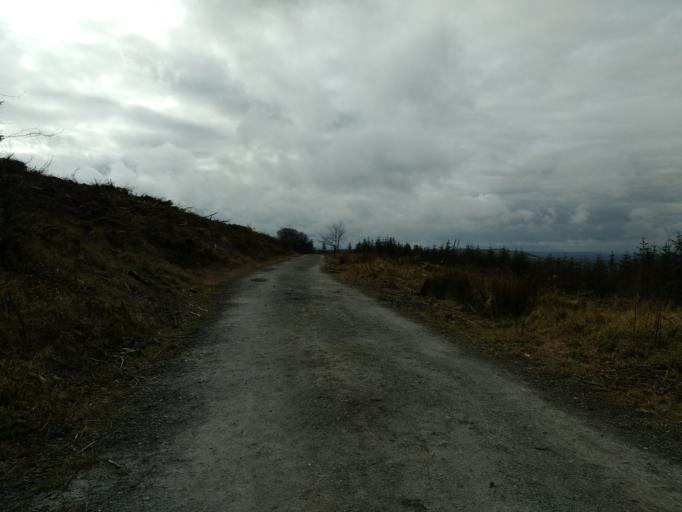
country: IE
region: Leinster
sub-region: Kilkenny
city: Callan
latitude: 52.6648
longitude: -7.5292
